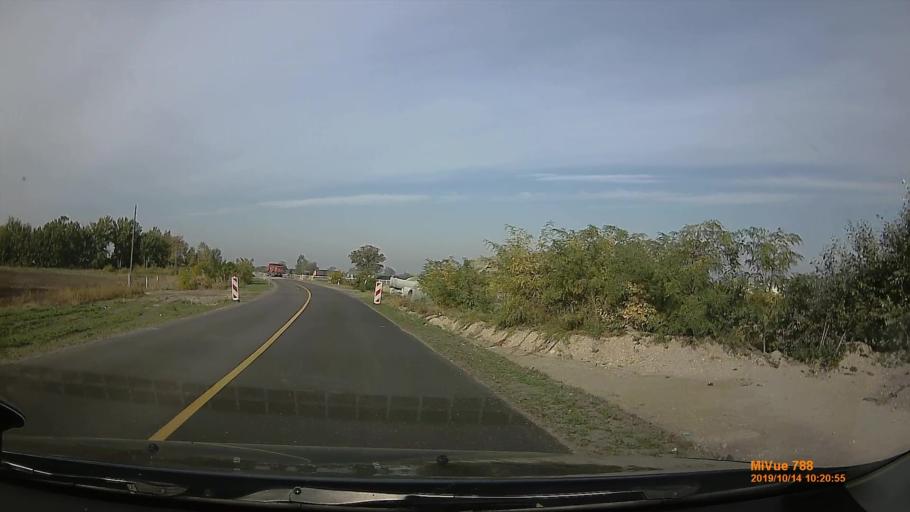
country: HU
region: Pest
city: Tortel
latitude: 47.1907
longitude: 19.9183
